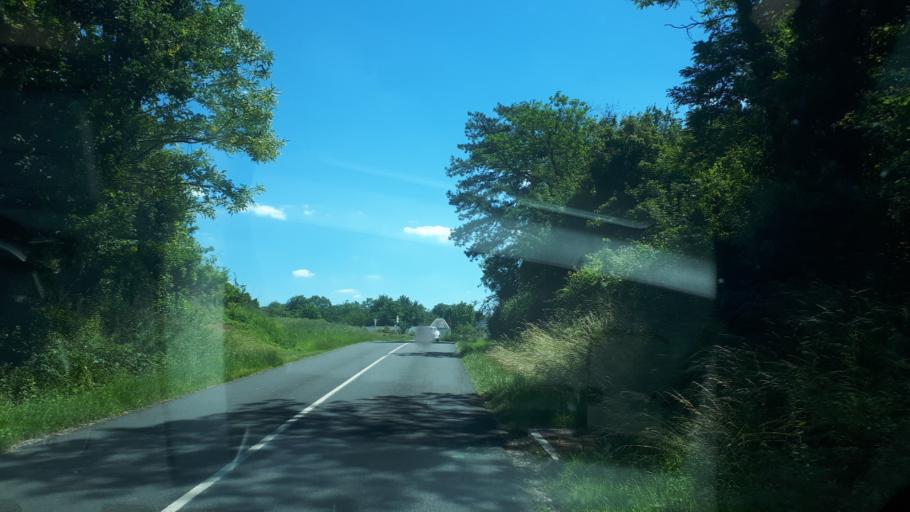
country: FR
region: Centre
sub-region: Departement du Loir-et-Cher
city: Chouzy-sur-Cisse
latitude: 47.5657
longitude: 1.2163
